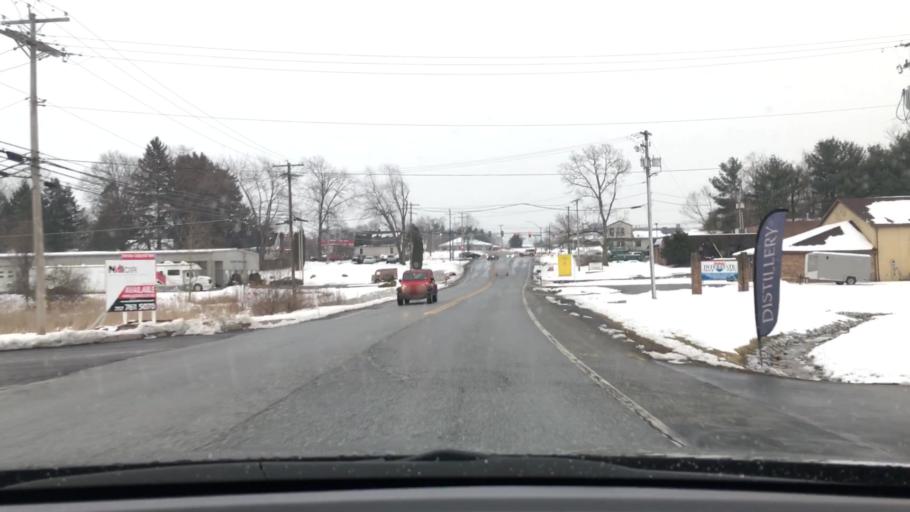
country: US
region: Pennsylvania
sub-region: York County
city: Valley Green
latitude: 40.1664
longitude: -76.8327
